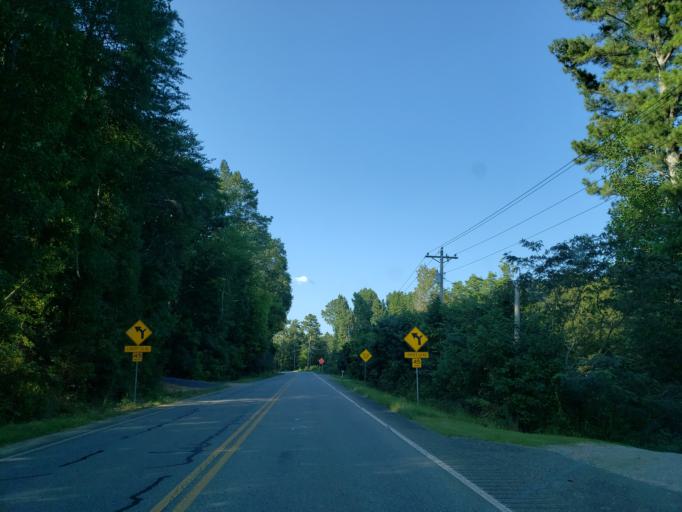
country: US
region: Tennessee
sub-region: Bradley County
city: Wildwood Lake
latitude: 34.9765
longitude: -84.7312
